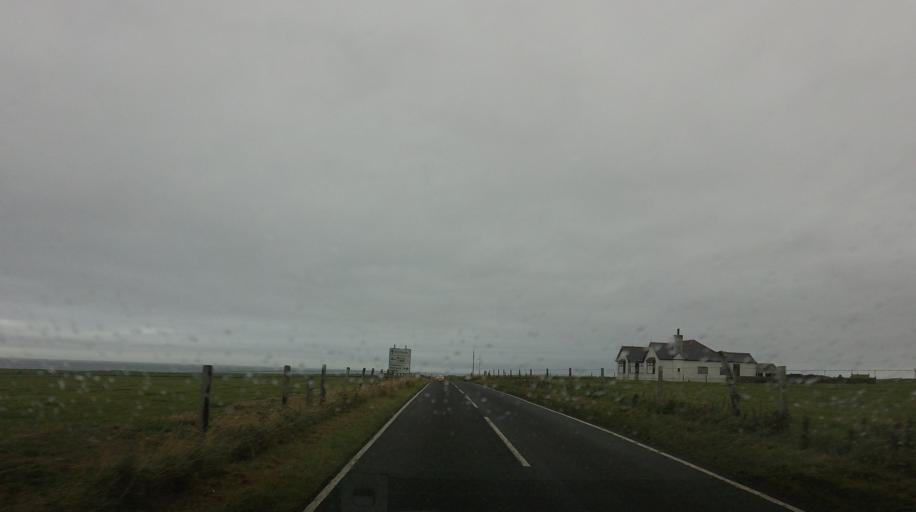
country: GB
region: Scotland
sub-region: Orkney Islands
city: Stromness
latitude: 59.1301
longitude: -3.3032
